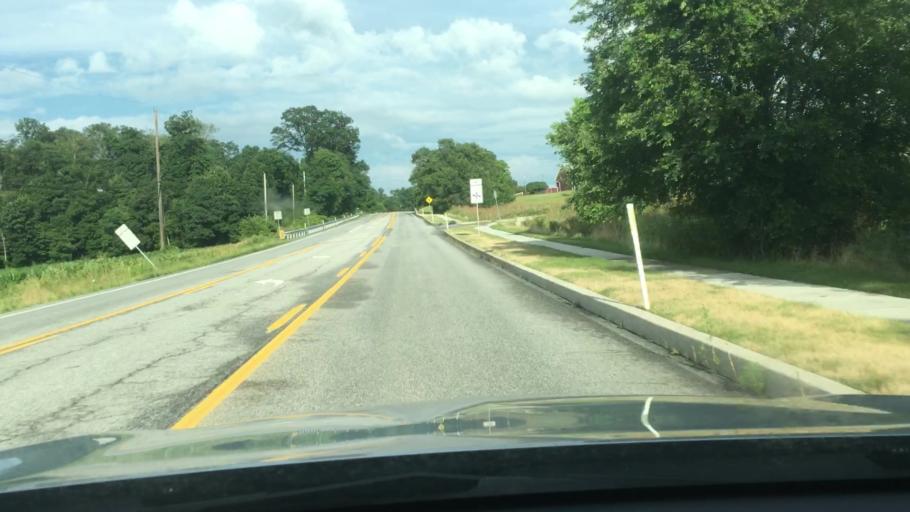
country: US
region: Pennsylvania
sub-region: York County
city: Dillsburg
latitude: 40.1052
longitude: -77.0206
